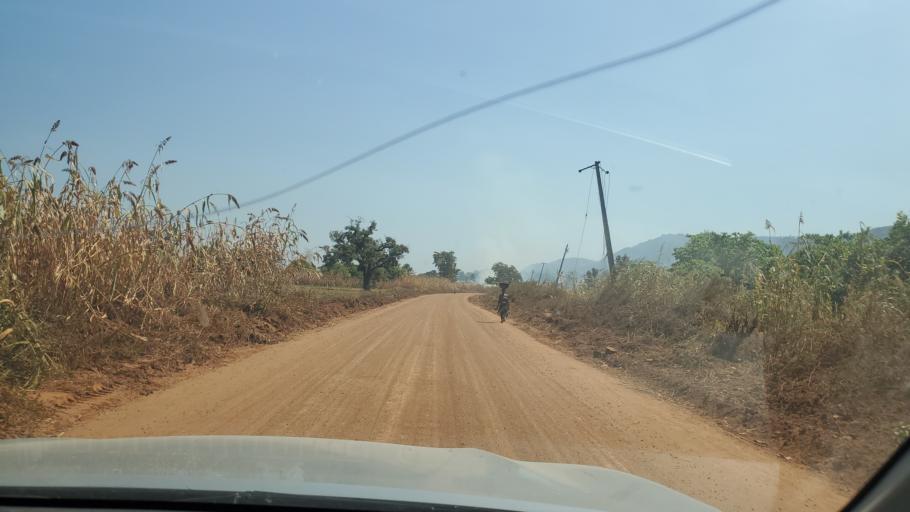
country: NG
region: Niger
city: Gawu Babangida
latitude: 9.2209
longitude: 6.8409
